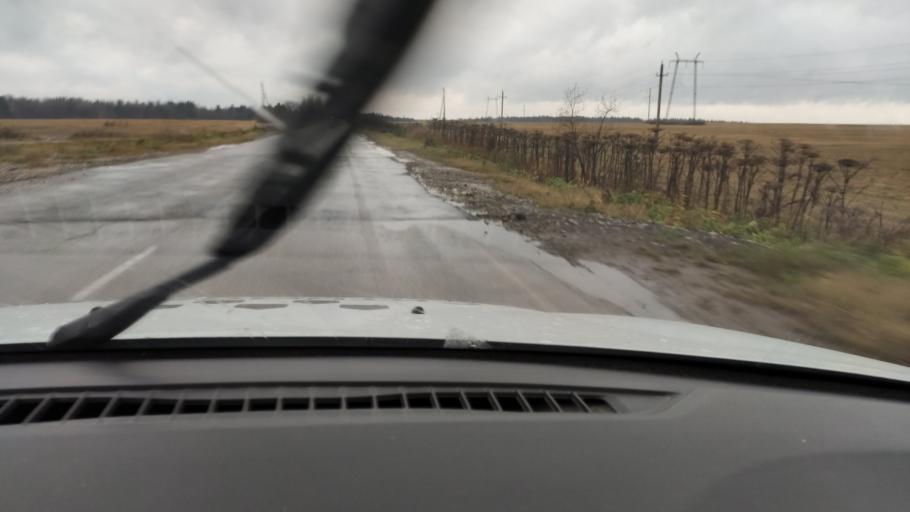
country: RU
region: Perm
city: Sylva
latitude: 58.0292
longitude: 56.7009
